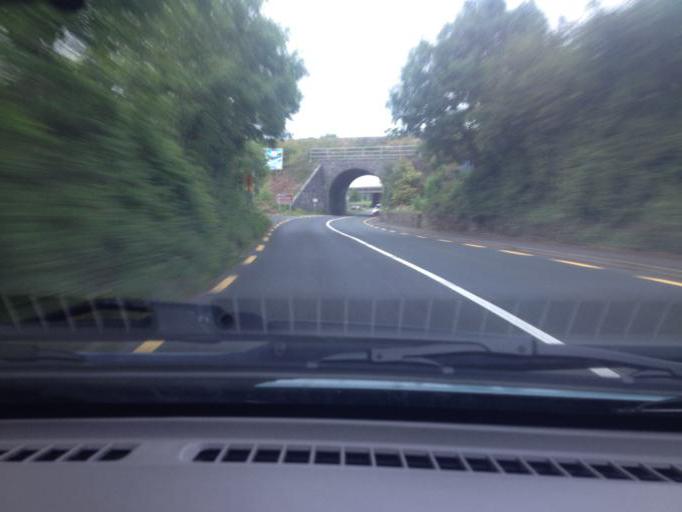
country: IE
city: Ballisodare
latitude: 54.2186
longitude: -8.5035
